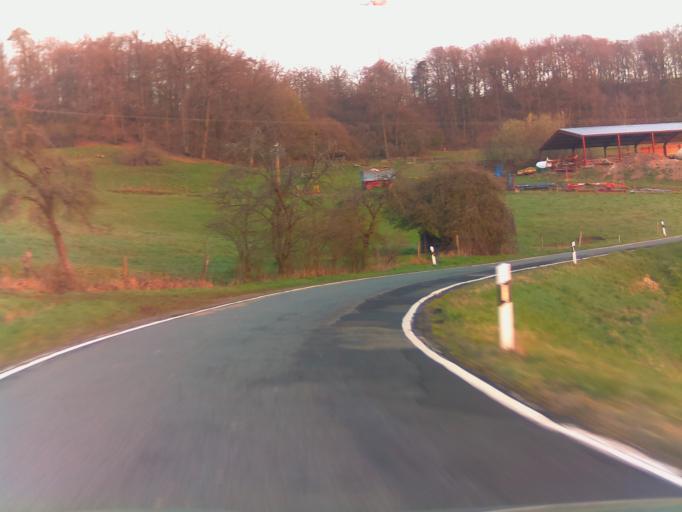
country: DE
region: Rheinland-Pfalz
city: Kirrweiler
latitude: 49.6427
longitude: 7.5005
